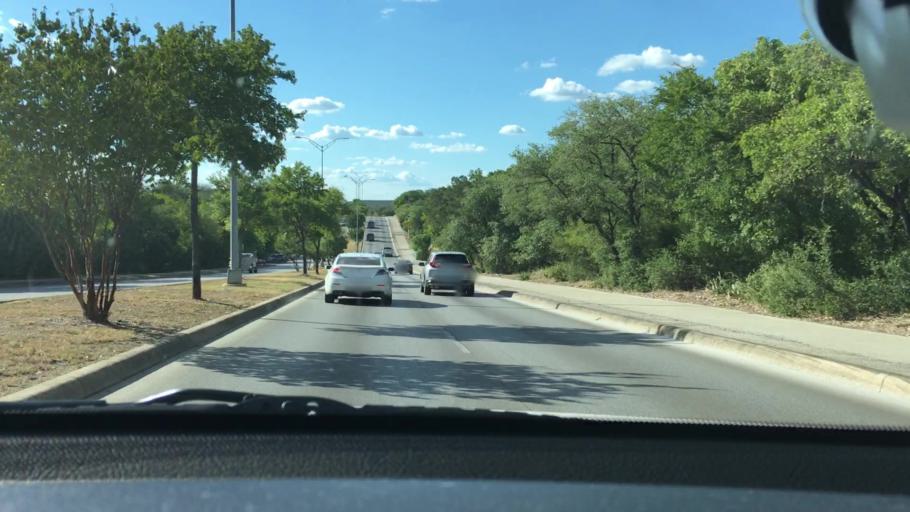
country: US
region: Texas
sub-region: Bexar County
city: Selma
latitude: 29.5857
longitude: -98.2871
